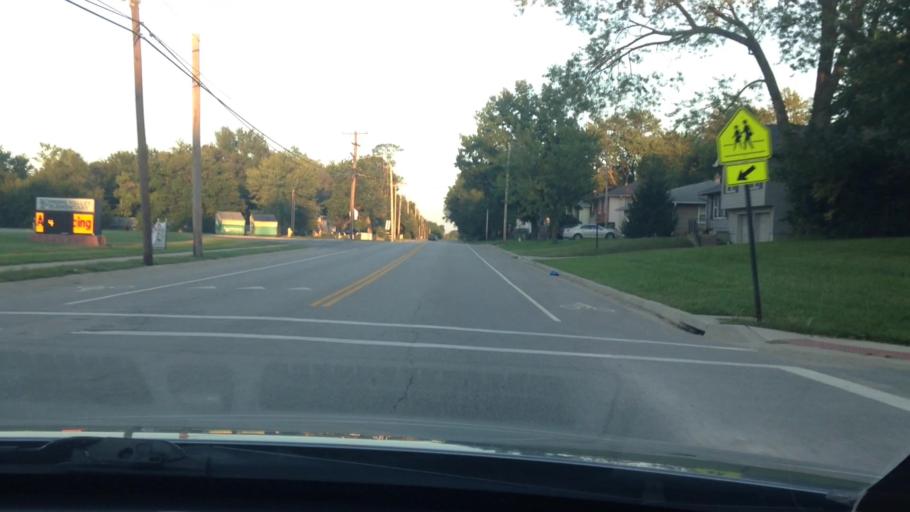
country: US
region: Missouri
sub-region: Jackson County
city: Raytown
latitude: 38.9731
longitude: -94.4809
